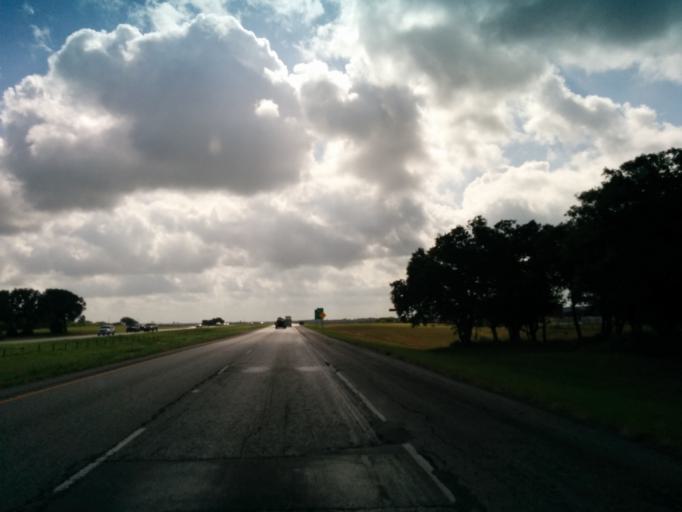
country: US
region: Texas
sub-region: Gonzales County
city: Waelder
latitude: 29.6573
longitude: -97.4235
